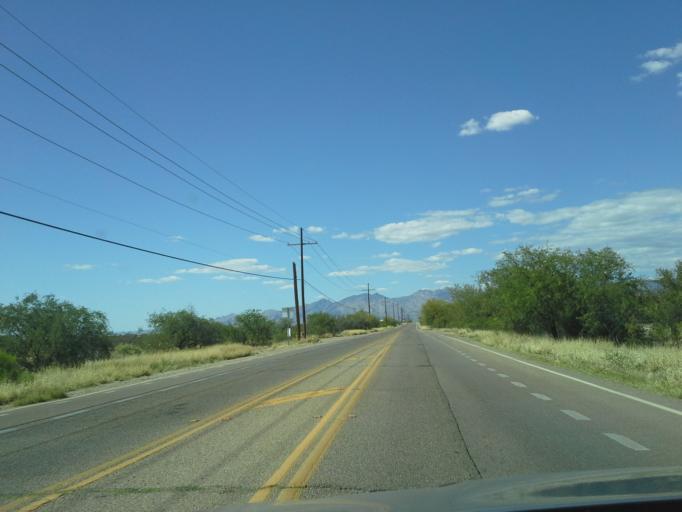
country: US
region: Arizona
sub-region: Pima County
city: Summit
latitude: 32.1254
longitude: -110.8580
